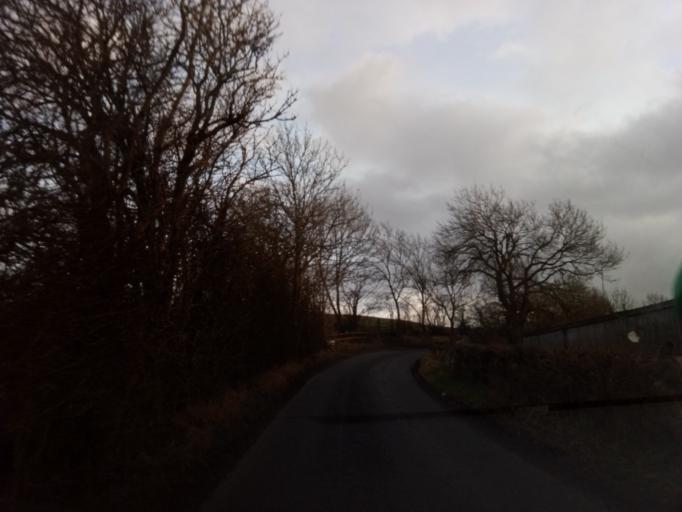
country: GB
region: Scotland
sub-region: The Scottish Borders
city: Selkirk
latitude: 55.5688
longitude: -2.8083
